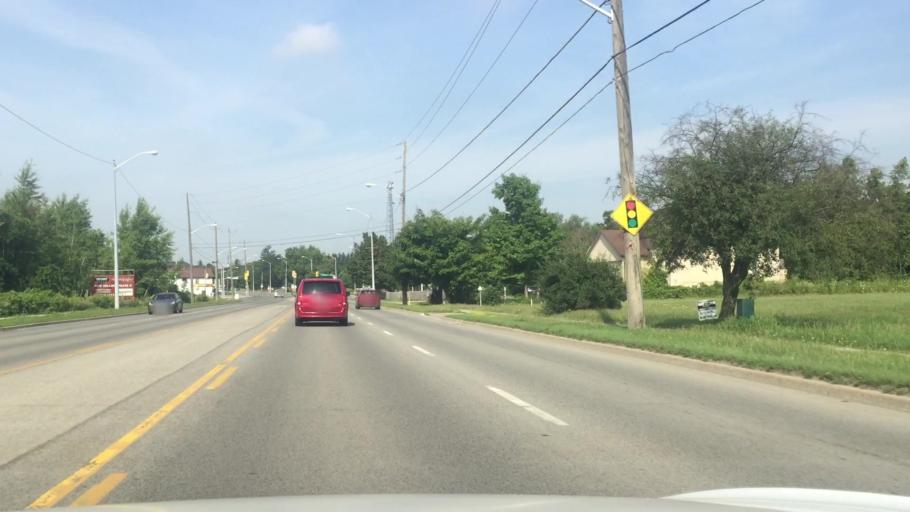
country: CA
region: Ontario
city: Oshawa
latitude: 43.9110
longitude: -78.7854
